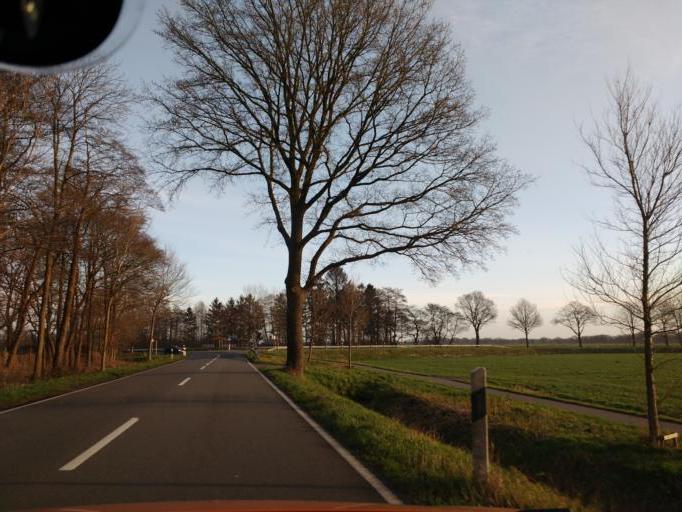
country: DE
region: Lower Saxony
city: Hatten
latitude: 53.1300
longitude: 8.3351
